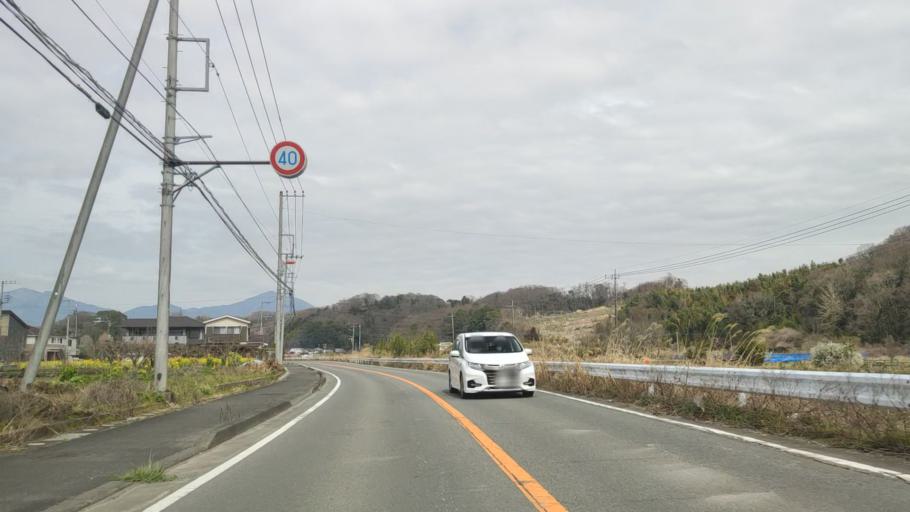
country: JP
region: Kanagawa
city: Ninomiya
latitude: 35.3251
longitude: 139.2190
